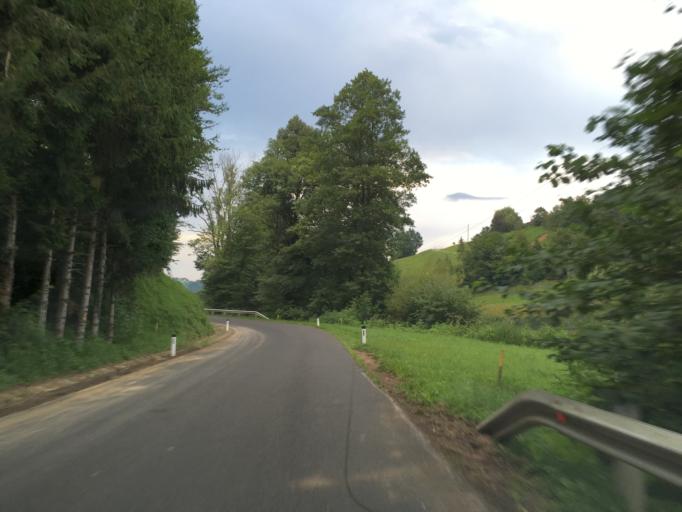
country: AT
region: Styria
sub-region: Politischer Bezirk Leibnitz
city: Oberhaag
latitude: 46.6761
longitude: 15.3522
